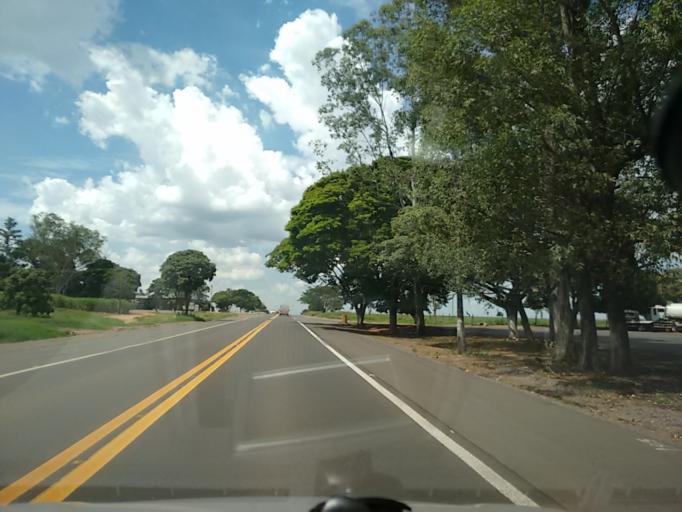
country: BR
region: Sao Paulo
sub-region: Osvaldo Cruz
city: Osvaldo Cruz
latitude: -21.9189
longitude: -50.8987
